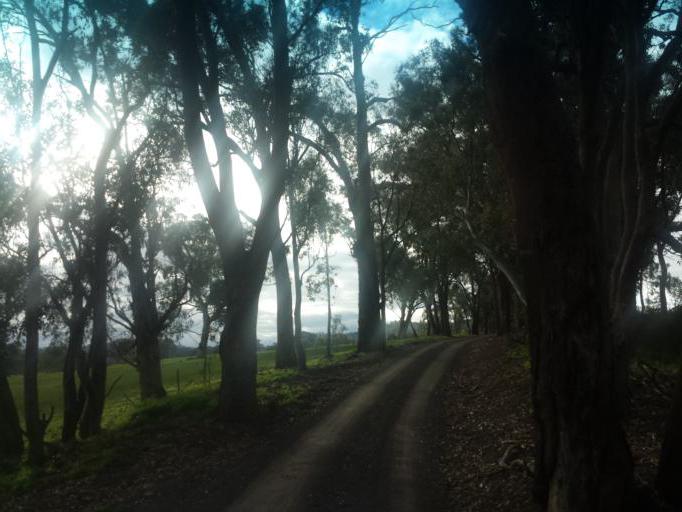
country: AU
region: Victoria
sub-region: Murrindindi
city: Kinglake West
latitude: -37.0315
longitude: 145.2502
